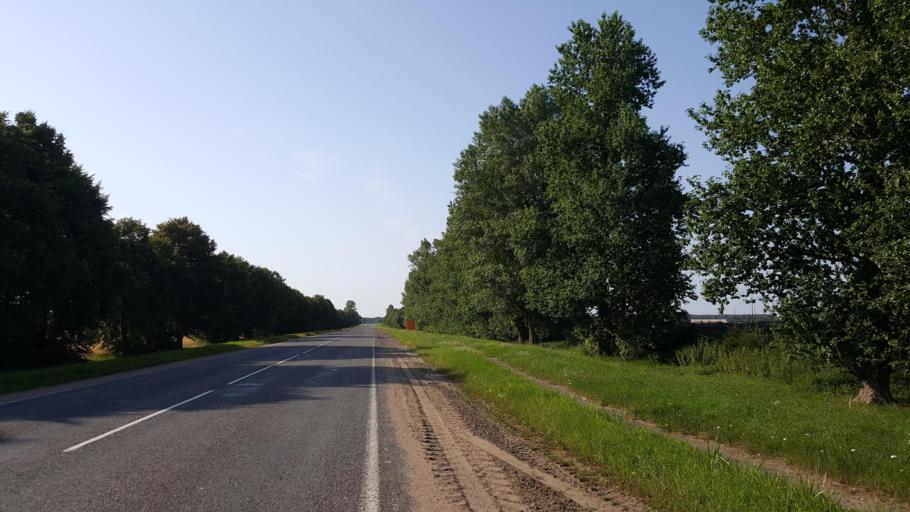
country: BY
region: Brest
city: Kamyanyets
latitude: 52.3576
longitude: 23.8943
